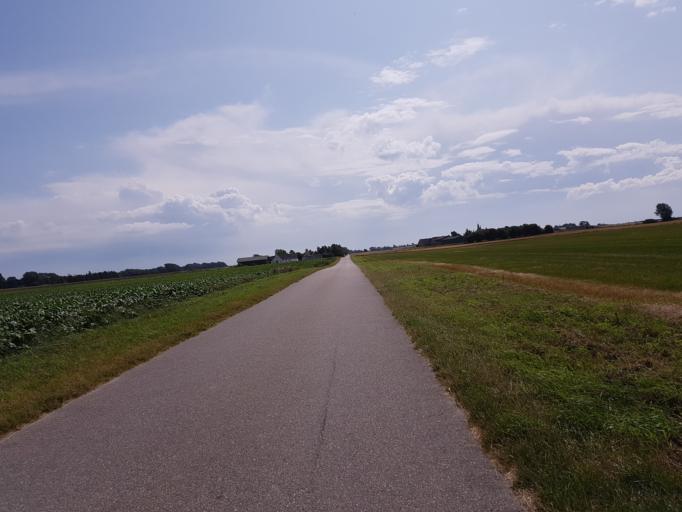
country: DK
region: Zealand
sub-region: Guldborgsund Kommune
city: Nykobing Falster
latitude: 54.5917
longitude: 11.9521
